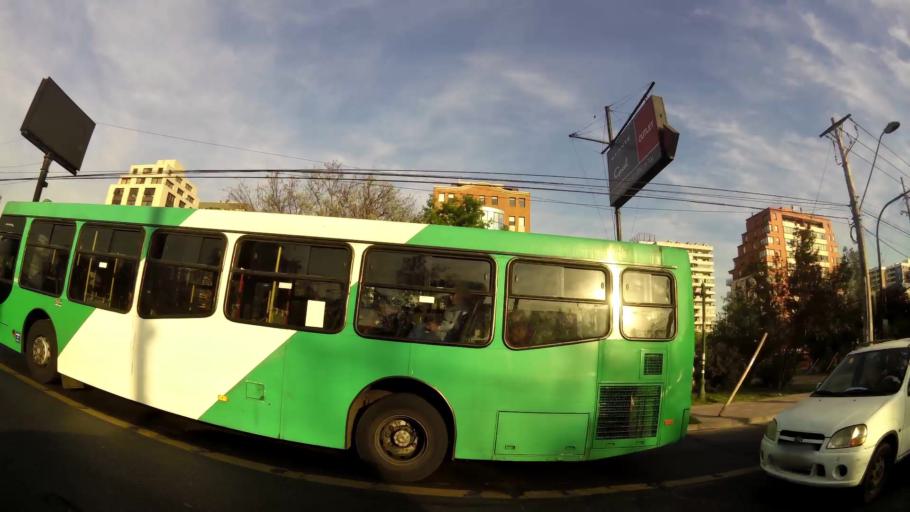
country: CL
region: Santiago Metropolitan
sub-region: Provincia de Santiago
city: Santiago
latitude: -33.4903
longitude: -70.6514
